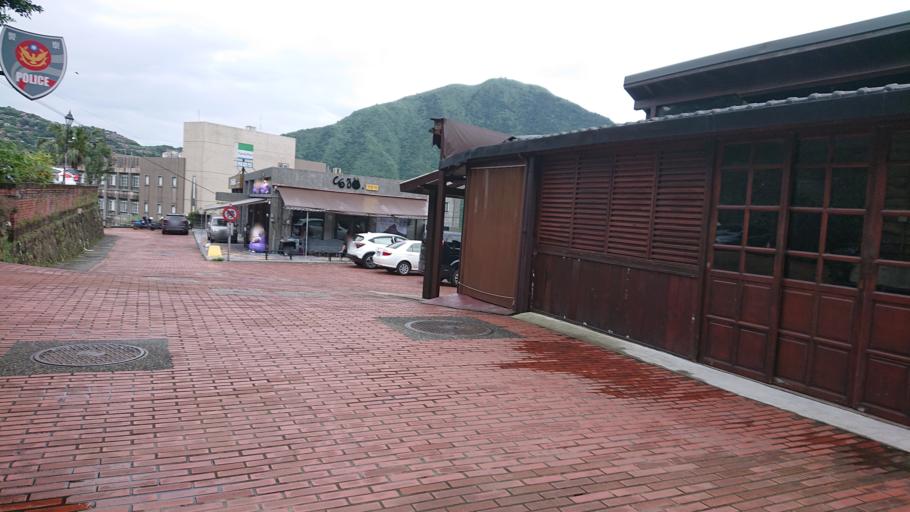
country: TW
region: Taiwan
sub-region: Keelung
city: Keelung
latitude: 25.1083
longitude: 121.8578
